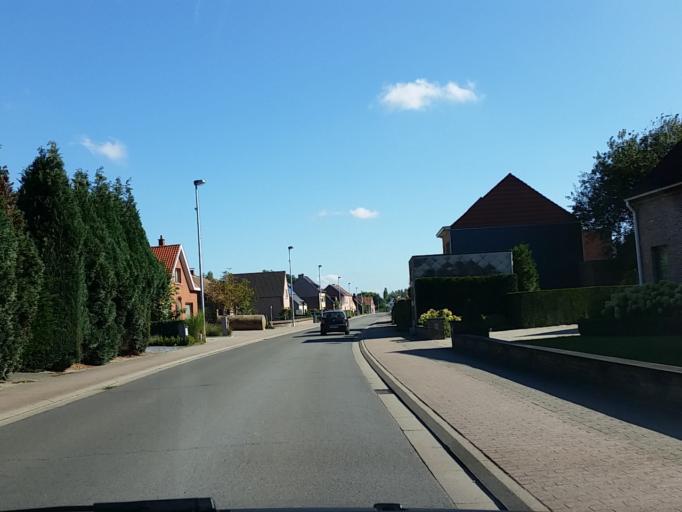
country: BE
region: Flanders
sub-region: Provincie Vlaams-Brabant
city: Boortmeerbeek
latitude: 50.9810
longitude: 4.5320
